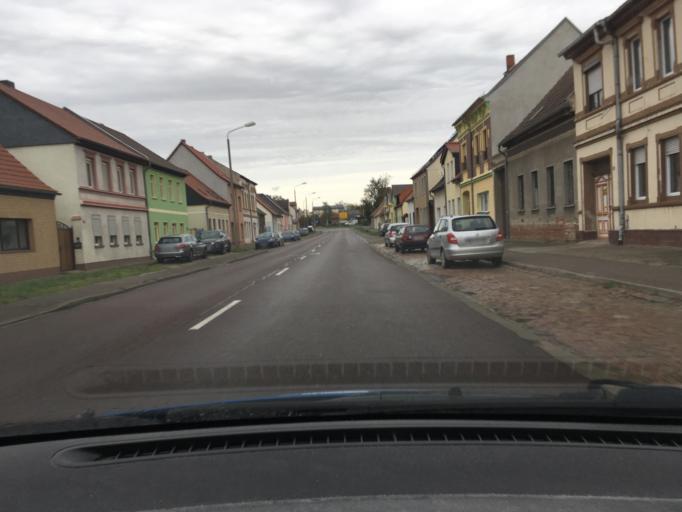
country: DE
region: Saxony-Anhalt
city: Zerbst
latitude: 51.9699
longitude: 12.0717
